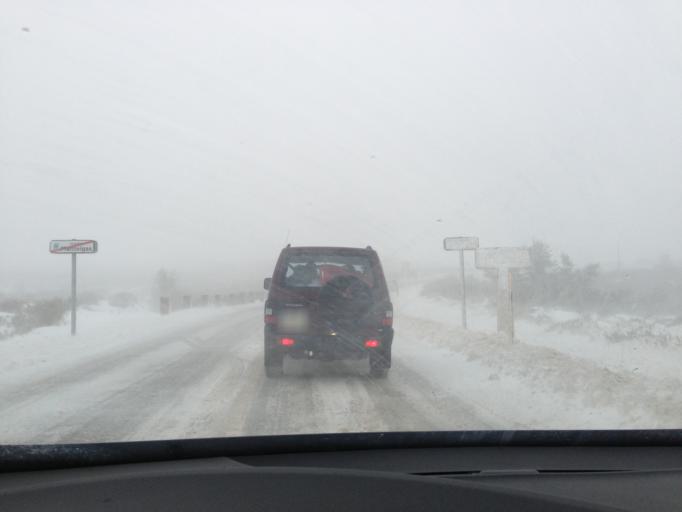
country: PT
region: Castelo Branco
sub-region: Covilha
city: Covilha
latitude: 40.3175
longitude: -7.5722
